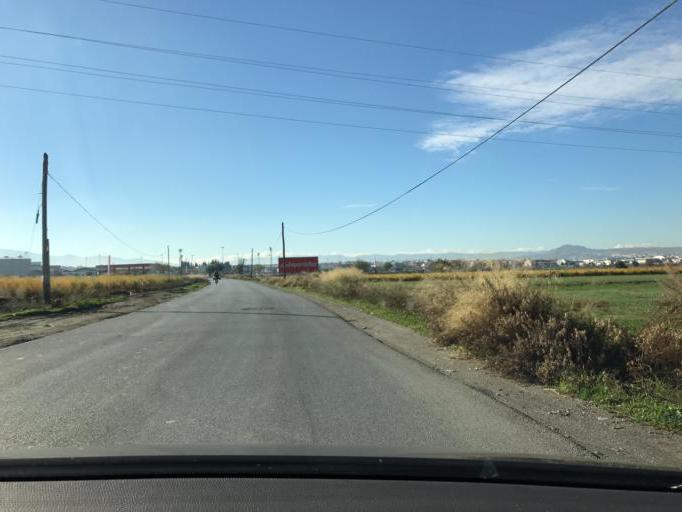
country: ES
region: Andalusia
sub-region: Provincia de Granada
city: Armilla
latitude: 37.1557
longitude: -3.6209
